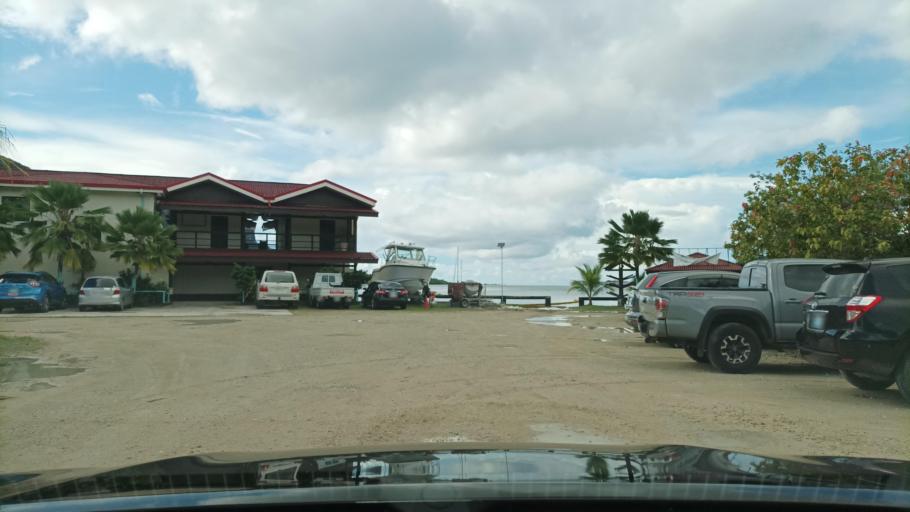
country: FM
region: Pohnpei
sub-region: Kolonia Municipality
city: Kolonia Town
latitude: 6.9589
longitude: 158.2014
